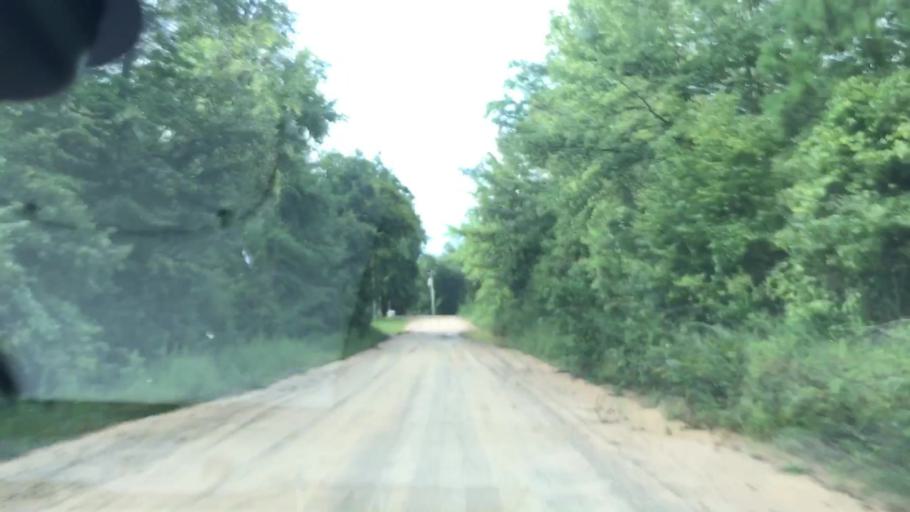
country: US
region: Georgia
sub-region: Clay County
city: Fort Gaines
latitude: 31.7226
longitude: -85.0747
